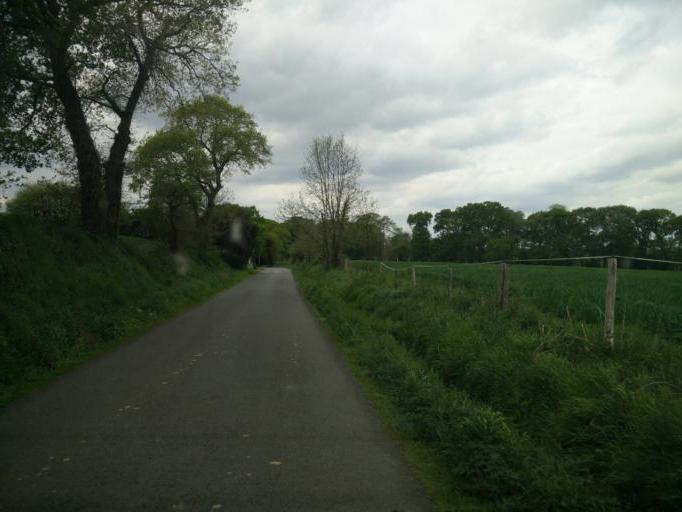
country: FR
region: Brittany
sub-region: Departement des Cotes-d'Armor
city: Hillion
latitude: 48.5163
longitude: -2.6520
